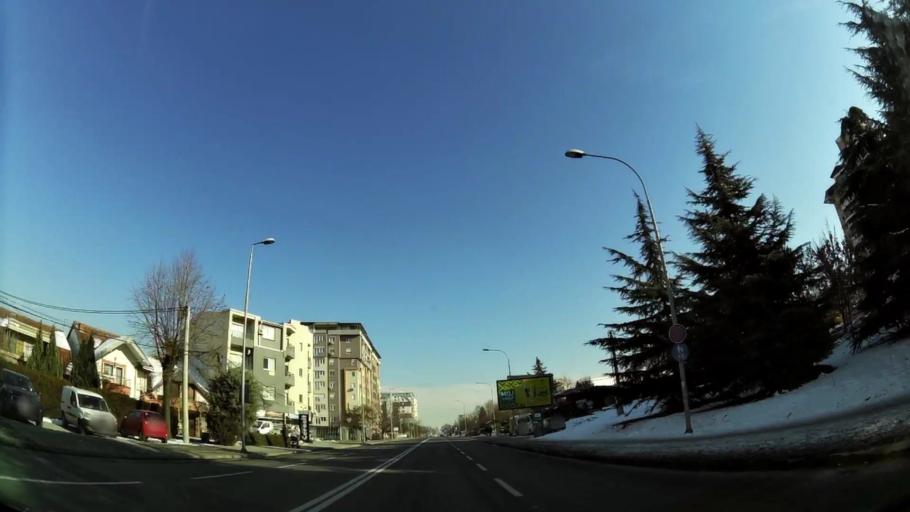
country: MK
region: Karpos
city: Skopje
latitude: 41.9980
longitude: 21.3929
